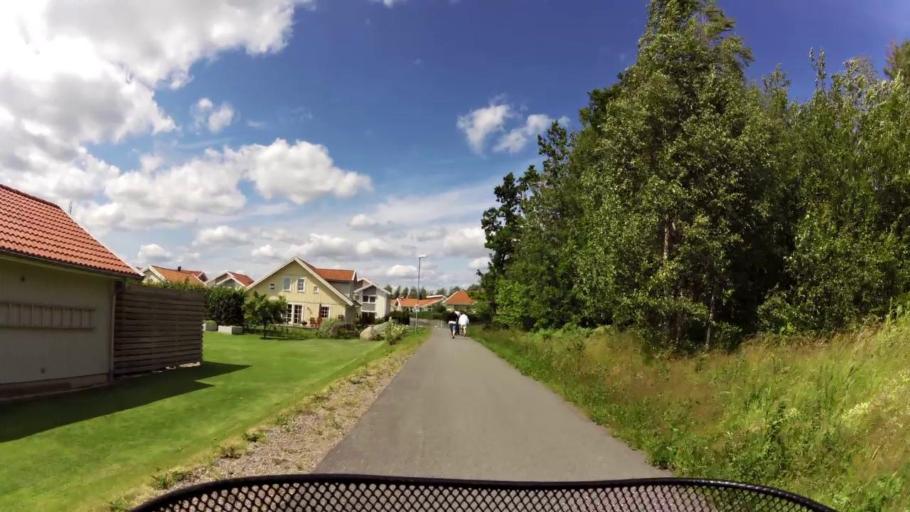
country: SE
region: OEstergoetland
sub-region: Linkopings Kommun
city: Ekangen
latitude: 58.4749
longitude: 15.6400
